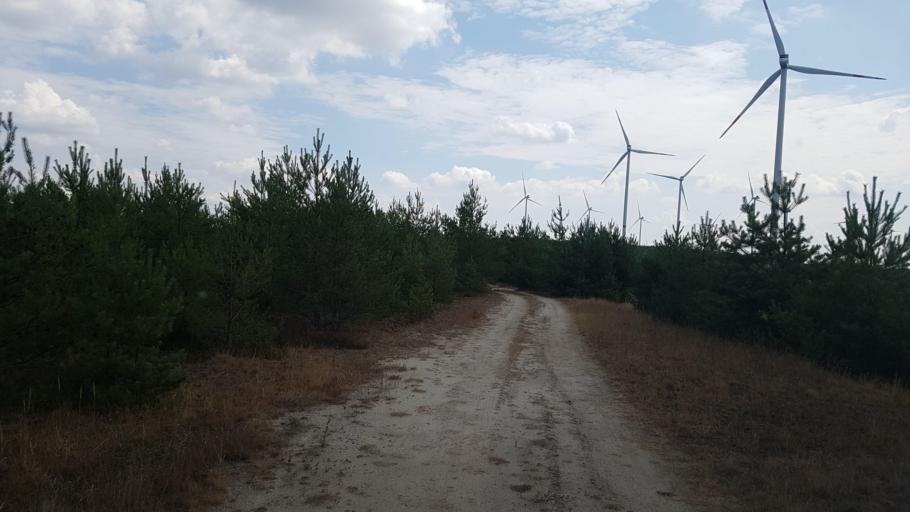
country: DE
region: Brandenburg
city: Sallgast
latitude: 51.5593
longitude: 13.8505
